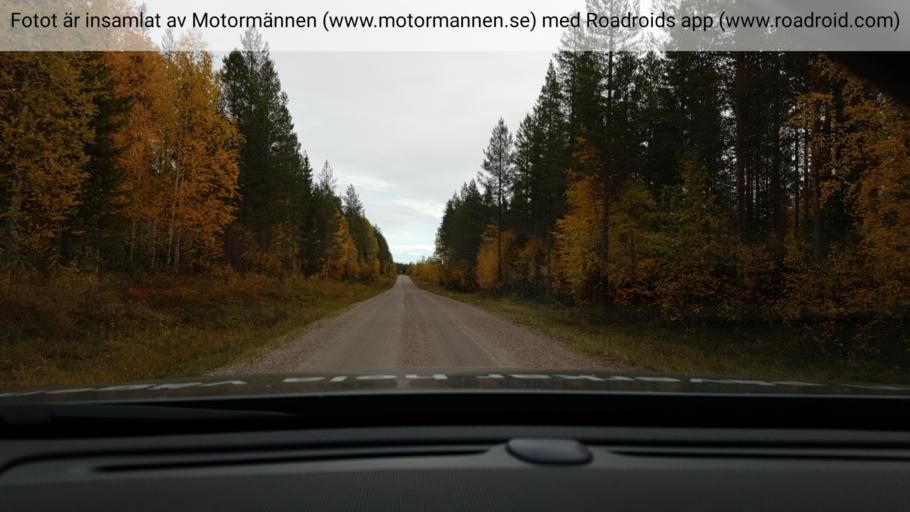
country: SE
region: Norrbotten
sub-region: Overkalix Kommun
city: OEverkalix
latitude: 66.2684
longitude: 23.0058
